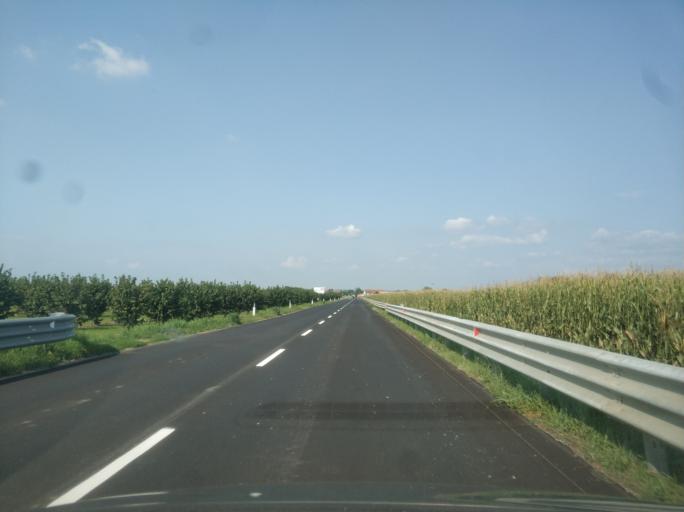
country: IT
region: Piedmont
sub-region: Provincia di Cuneo
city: Cervere
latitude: 44.6213
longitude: 7.7801
